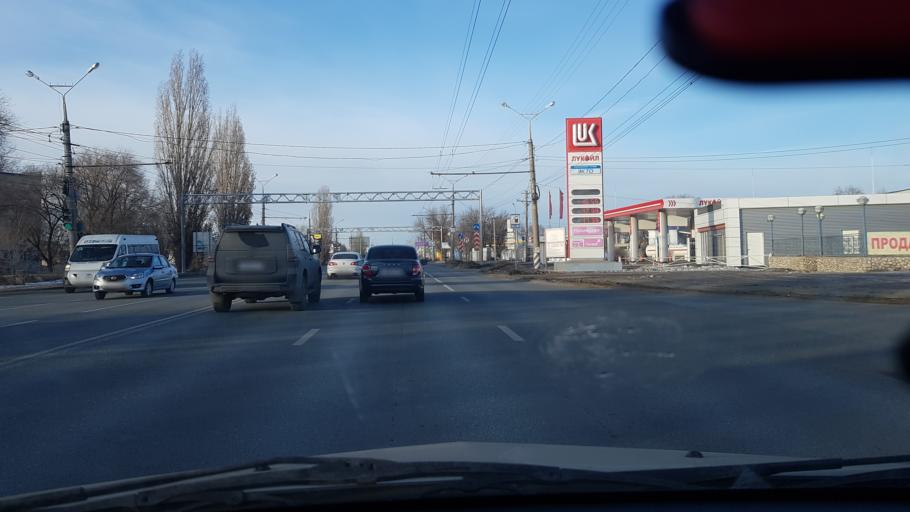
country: RU
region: Samara
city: Tol'yatti
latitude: 53.5359
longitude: 49.3942
